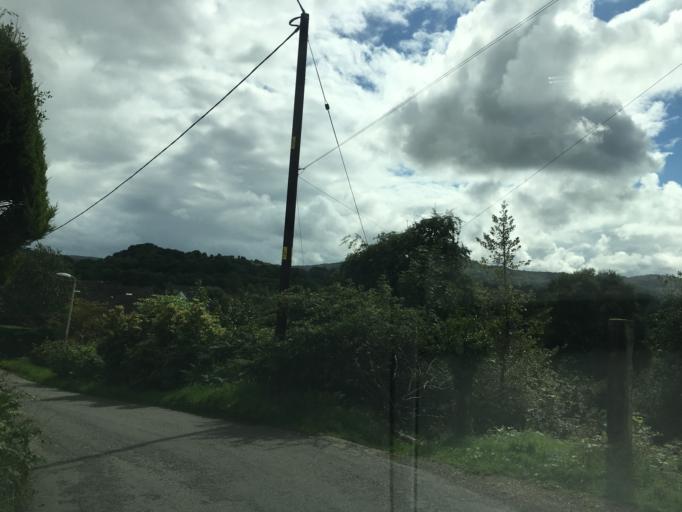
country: GB
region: Scotland
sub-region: Argyll and Bute
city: Oban
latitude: 56.4348
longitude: -5.2350
